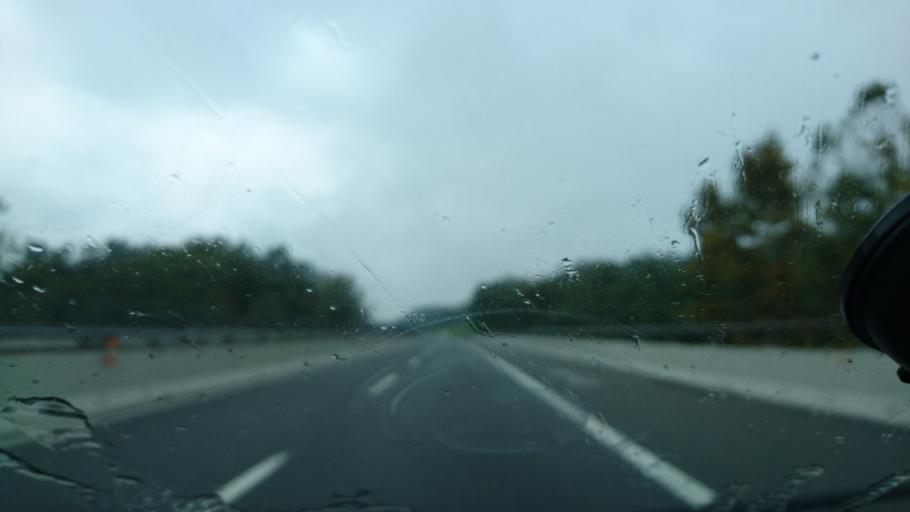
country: IT
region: Piedmont
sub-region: Provincia di Novara
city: Cressa
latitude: 45.6644
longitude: 8.5138
